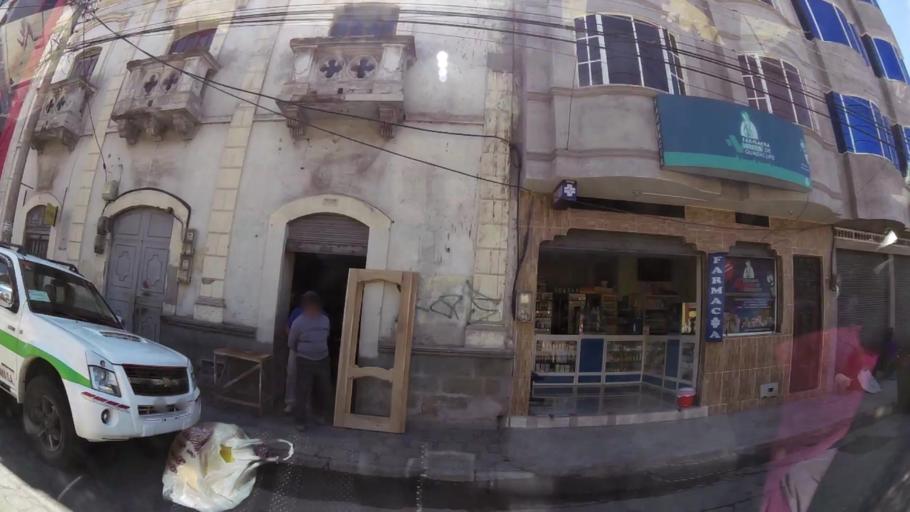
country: EC
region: Chimborazo
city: Riobamba
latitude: -1.6747
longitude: -78.6552
